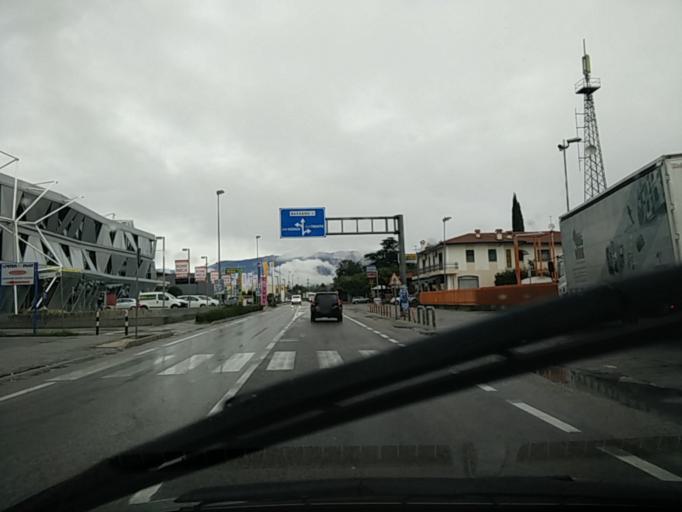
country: IT
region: Veneto
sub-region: Provincia di Vicenza
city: San Zeno-San Giuseppe
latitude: 45.7330
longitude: 11.7605
